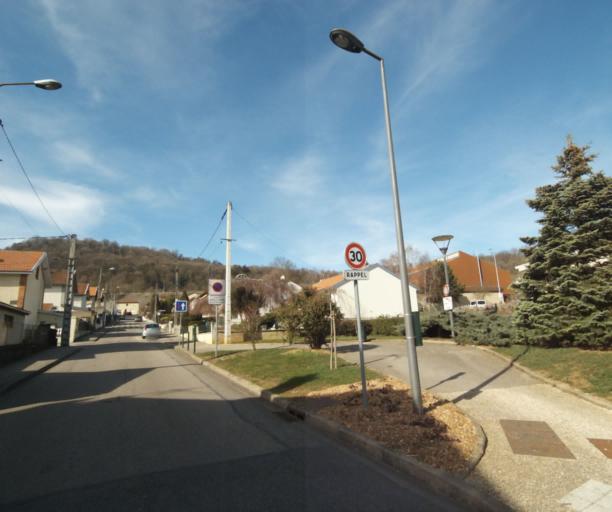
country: FR
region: Lorraine
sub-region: Departement de Meurthe-et-Moselle
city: Maxeville
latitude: 48.7169
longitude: 6.1675
